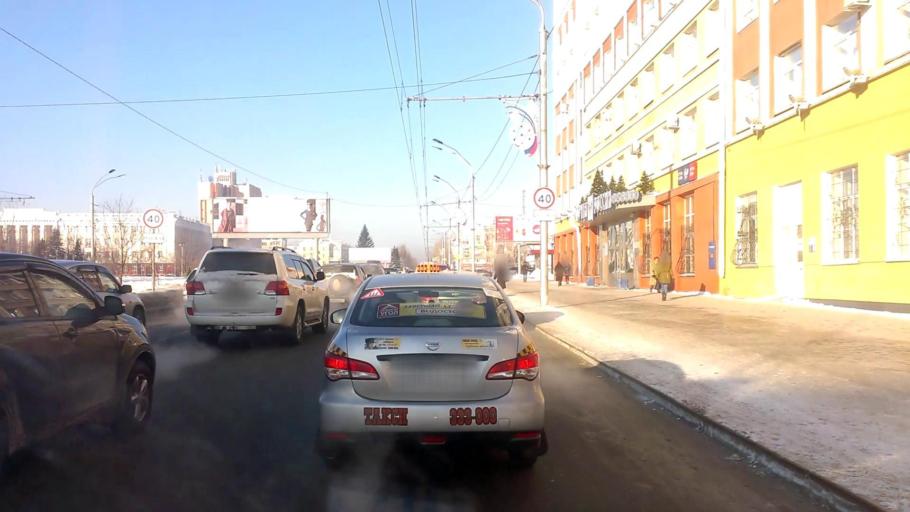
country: RU
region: Altai Krai
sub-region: Gorod Barnaulskiy
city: Barnaul
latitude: 53.3461
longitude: 83.7794
